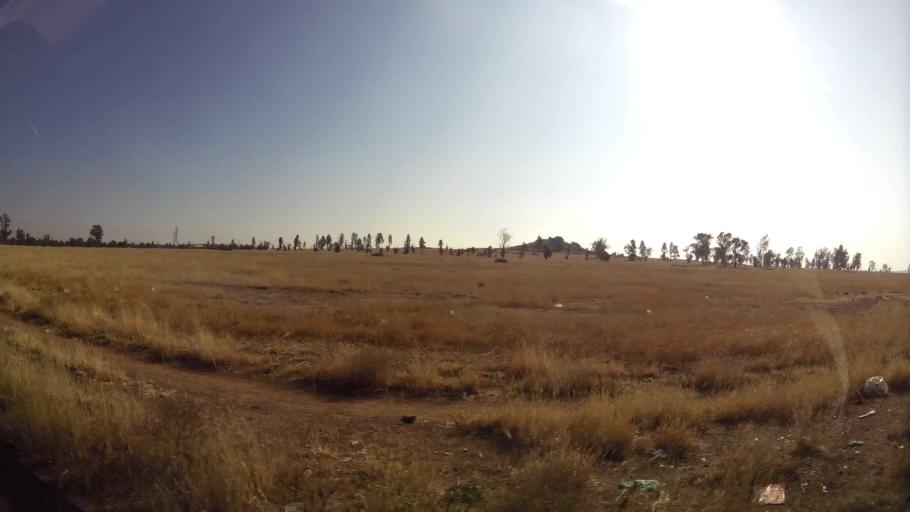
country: ZA
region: Orange Free State
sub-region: Mangaung Metropolitan Municipality
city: Bloemfontein
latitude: -29.1724
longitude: 26.2023
